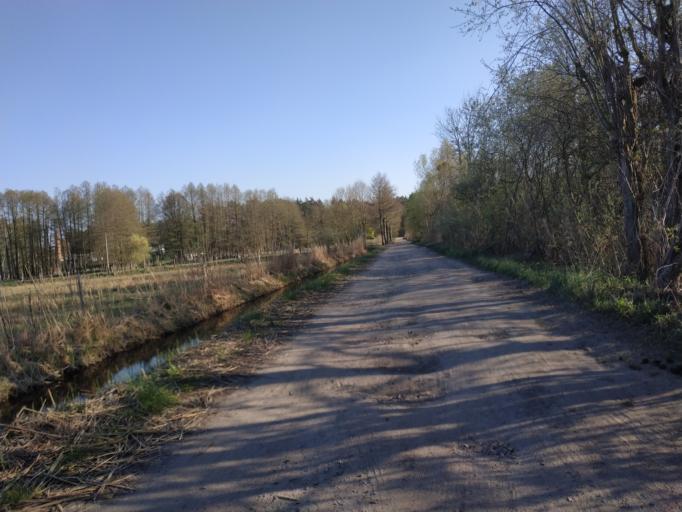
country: DE
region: Brandenburg
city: Strausberg
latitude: 52.5546
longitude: 13.8444
